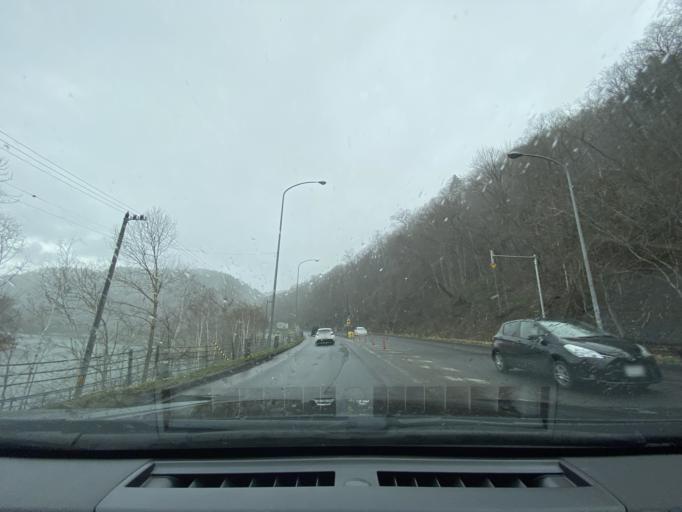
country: JP
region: Hokkaido
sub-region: Asahikawa-shi
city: Asahikawa
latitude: 43.7364
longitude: 142.2402
